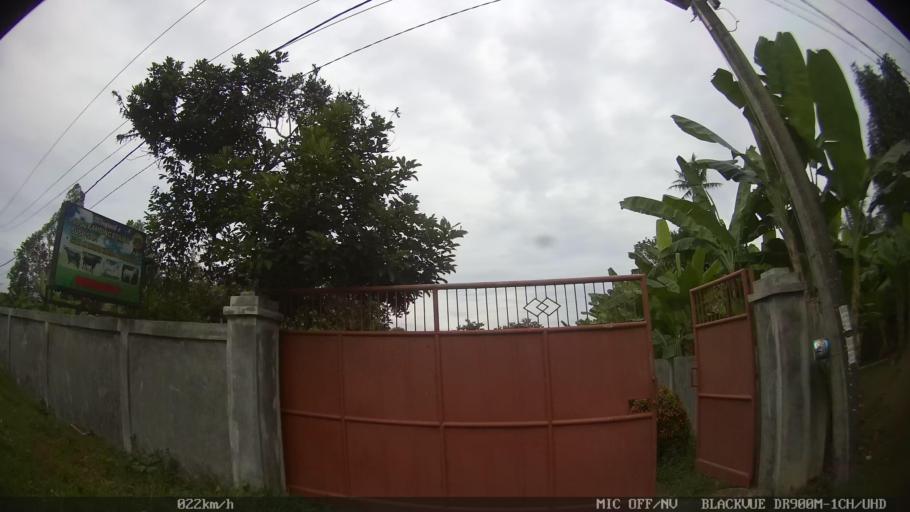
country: ID
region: North Sumatra
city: Sunggal
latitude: 3.6556
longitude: 98.5896
